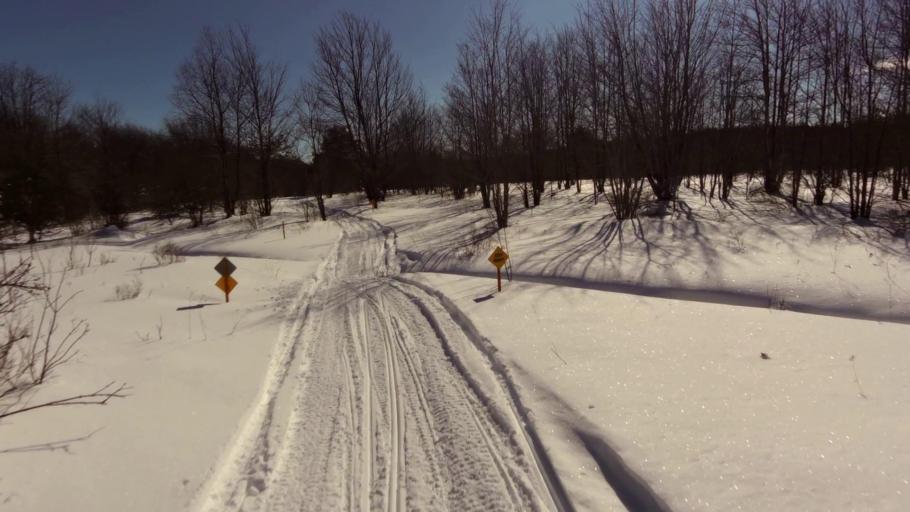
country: US
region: New York
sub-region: Cattaraugus County
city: Franklinville
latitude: 42.3451
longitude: -78.3776
